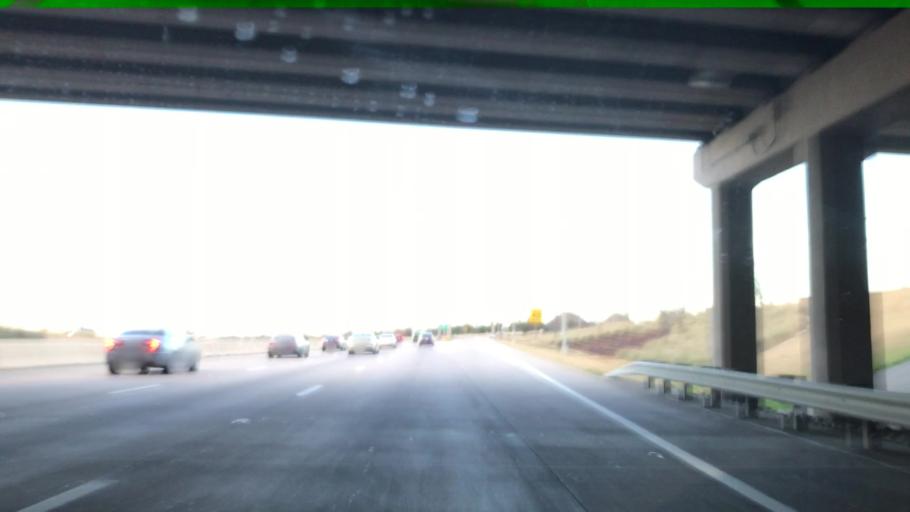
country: US
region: Texas
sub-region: Denton County
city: The Colony
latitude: 33.0357
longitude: -96.9245
